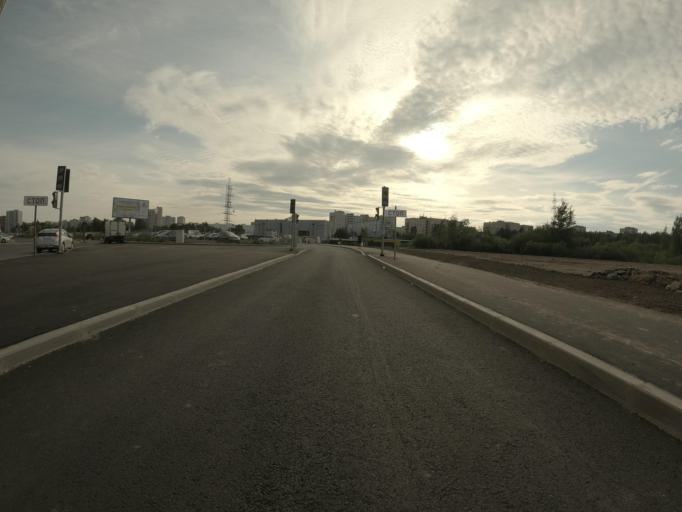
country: RU
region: St.-Petersburg
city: Krasnogvargeisky
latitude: 59.9189
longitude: 30.5057
